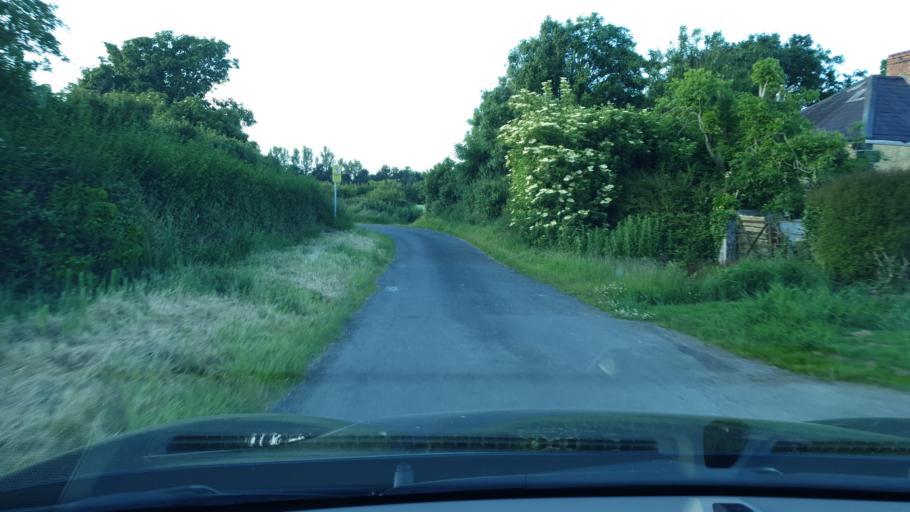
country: IE
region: Leinster
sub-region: Fingal County
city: Blanchardstown
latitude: 53.4445
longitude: -6.3937
